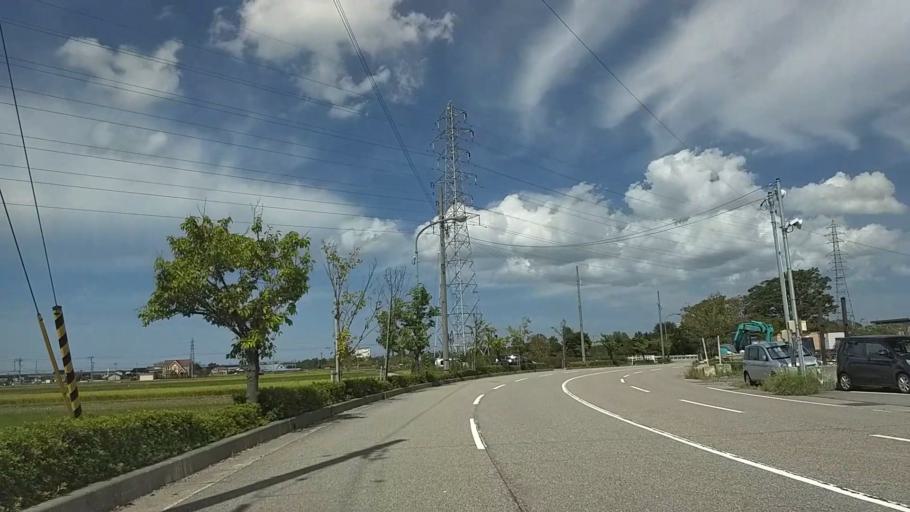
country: JP
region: Ishikawa
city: Kanazawa-shi
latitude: 36.5921
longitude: 136.6564
